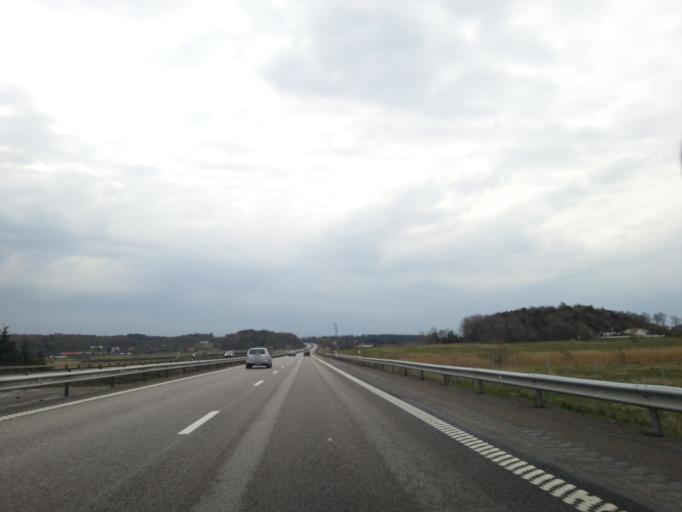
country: SE
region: Halland
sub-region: Kungsbacka Kommun
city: Kungsbacka
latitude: 57.4610
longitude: 12.0798
